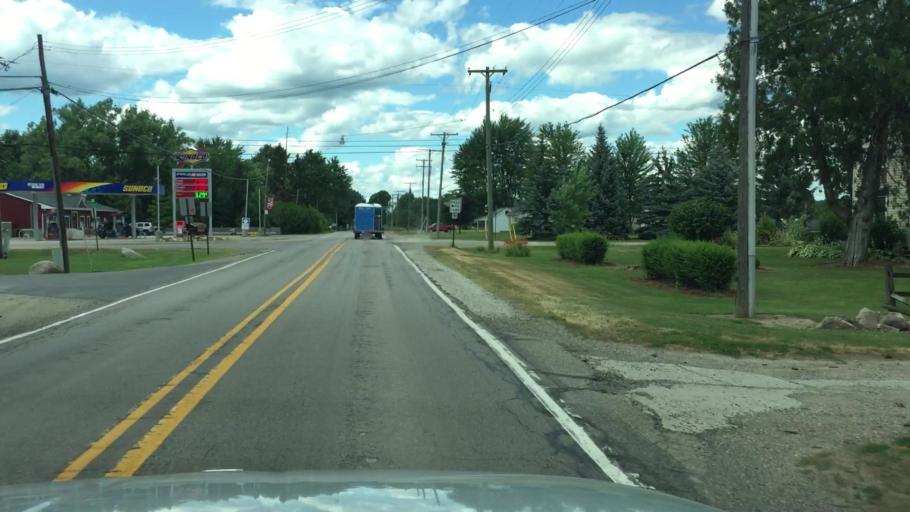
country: US
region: Michigan
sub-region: Saint Clair County
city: Capac
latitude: 42.9231
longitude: -82.9456
